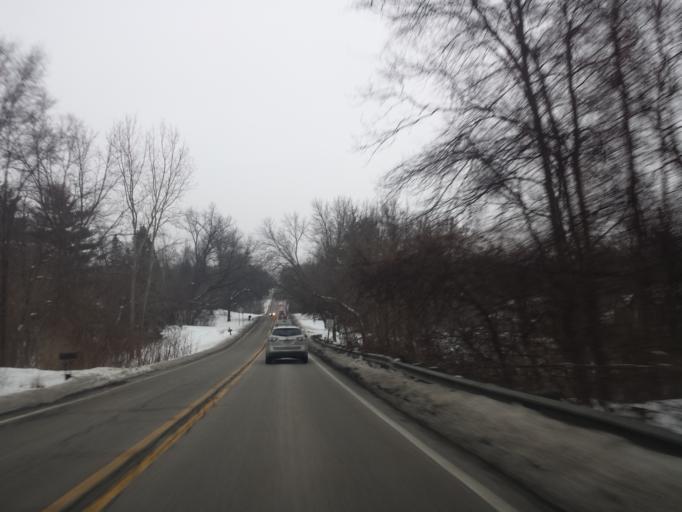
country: US
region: Michigan
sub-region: Oakland County
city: Orchard Lake
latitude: 42.5546
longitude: -83.3416
